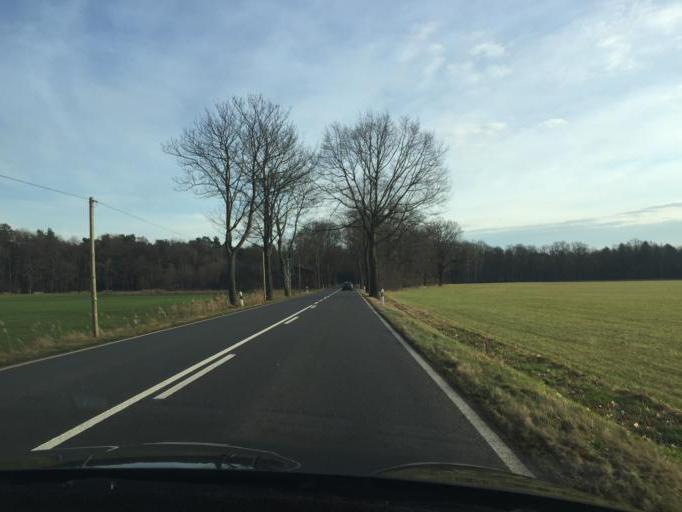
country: DE
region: Brandenburg
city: Cottbus
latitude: 51.7335
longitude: 14.4186
